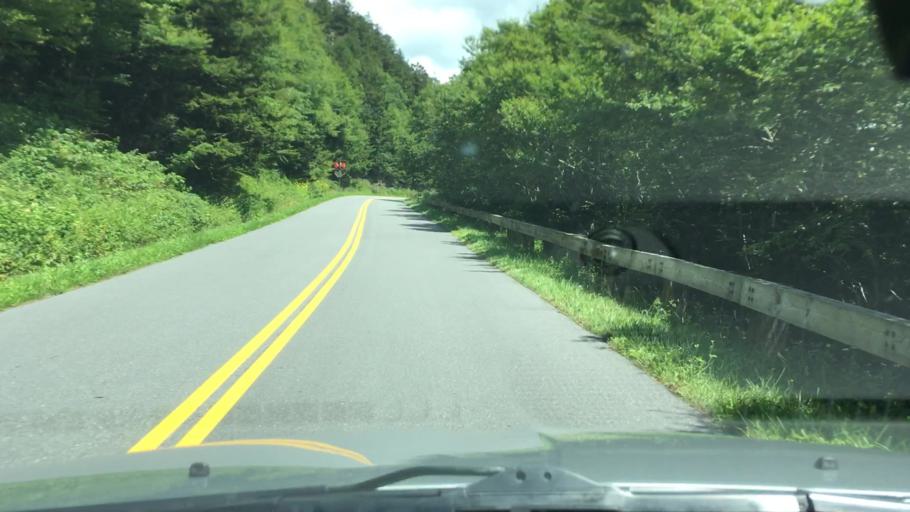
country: US
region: North Carolina
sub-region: Buncombe County
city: Black Mountain
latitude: 35.7349
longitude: -82.3221
